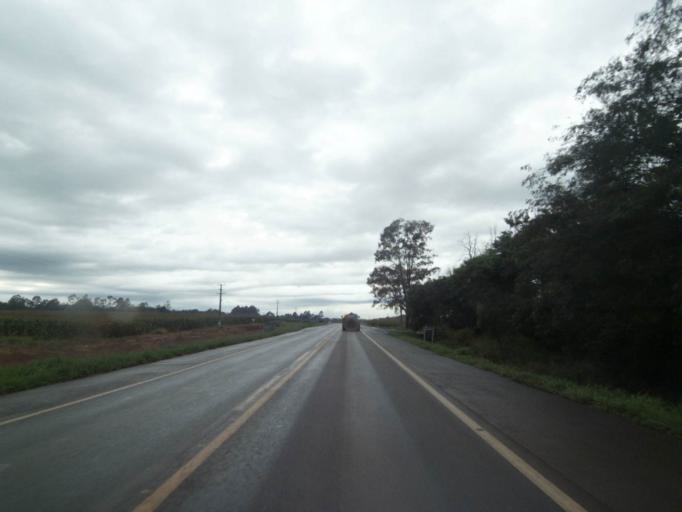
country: BR
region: Parana
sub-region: Toledo
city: Toledo
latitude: -24.6881
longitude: -53.7696
